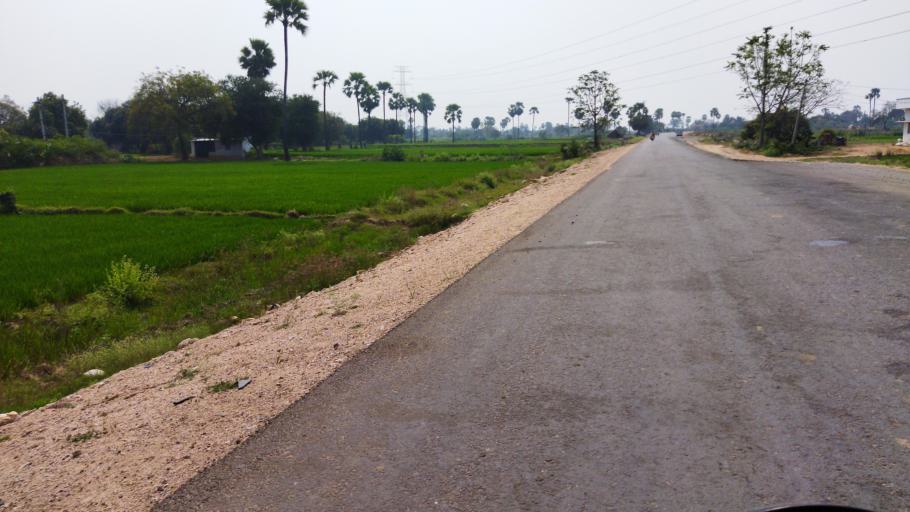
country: IN
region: Telangana
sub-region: Nalgonda
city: Nalgonda
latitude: 17.1158
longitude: 79.3619
